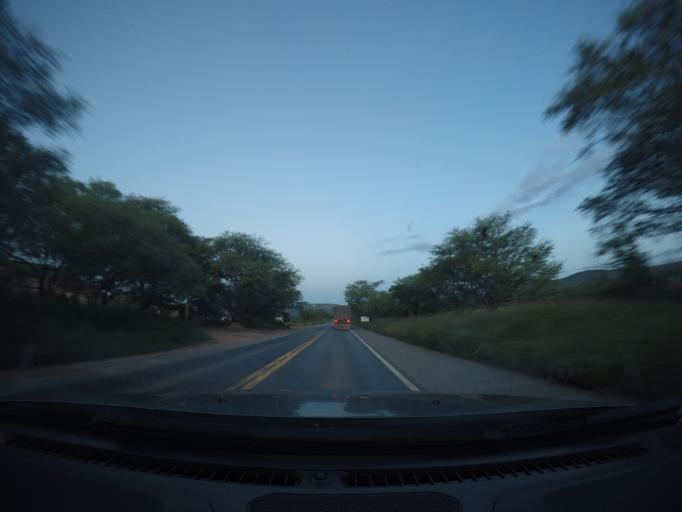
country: BR
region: Bahia
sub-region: Seabra
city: Seabra
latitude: -12.4876
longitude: -41.7279
